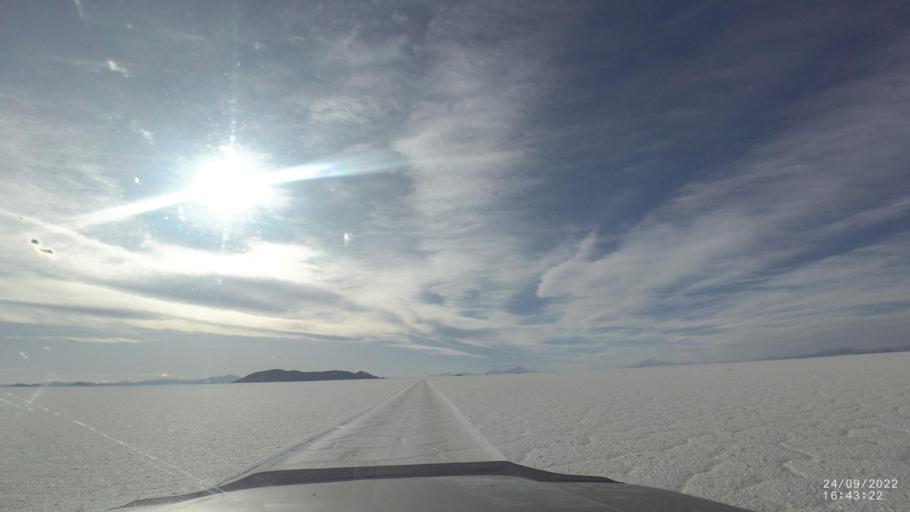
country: BO
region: Potosi
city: Colchani
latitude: -20.1663
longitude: -67.7455
